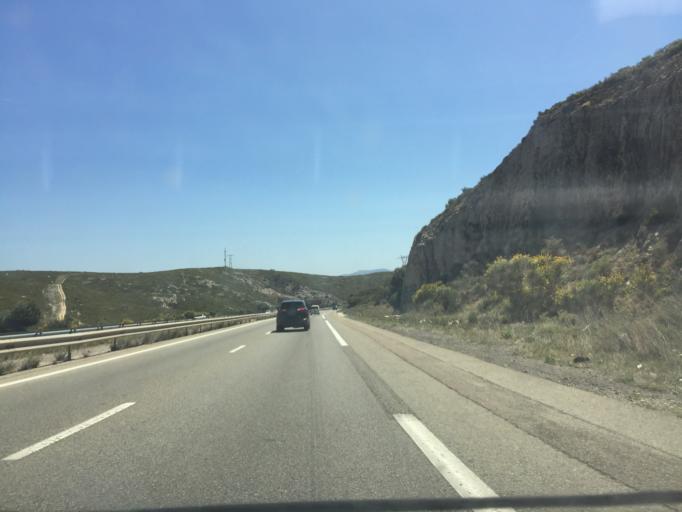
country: FR
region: Provence-Alpes-Cote d'Azur
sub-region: Departement des Bouches-du-Rhone
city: Marseille 16
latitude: 43.3772
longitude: 5.3179
